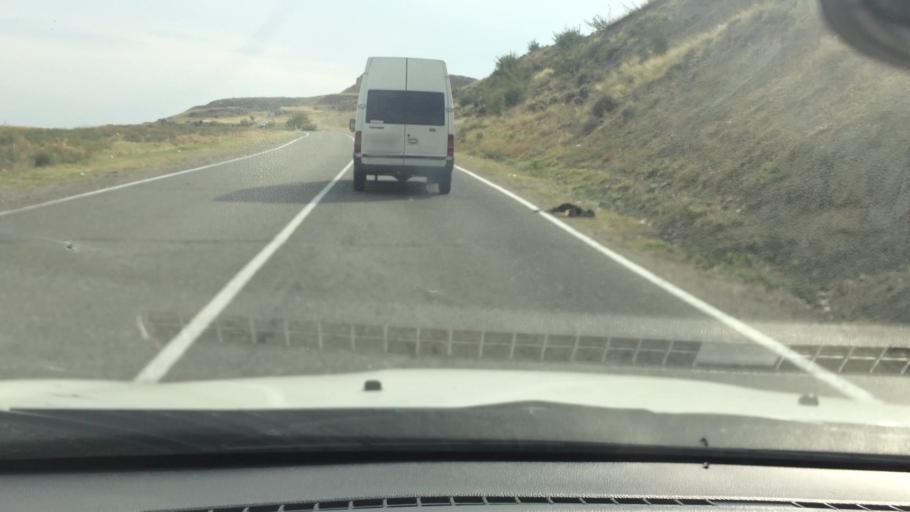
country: GE
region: Kvemo Kartli
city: Rust'avi
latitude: 41.5379
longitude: 44.9777
